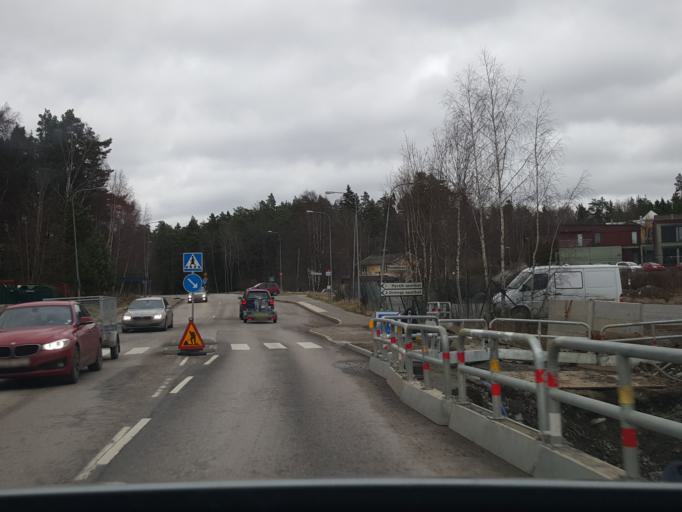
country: SE
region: Stockholm
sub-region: Nacka Kommun
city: Boo
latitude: 59.3288
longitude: 18.2817
